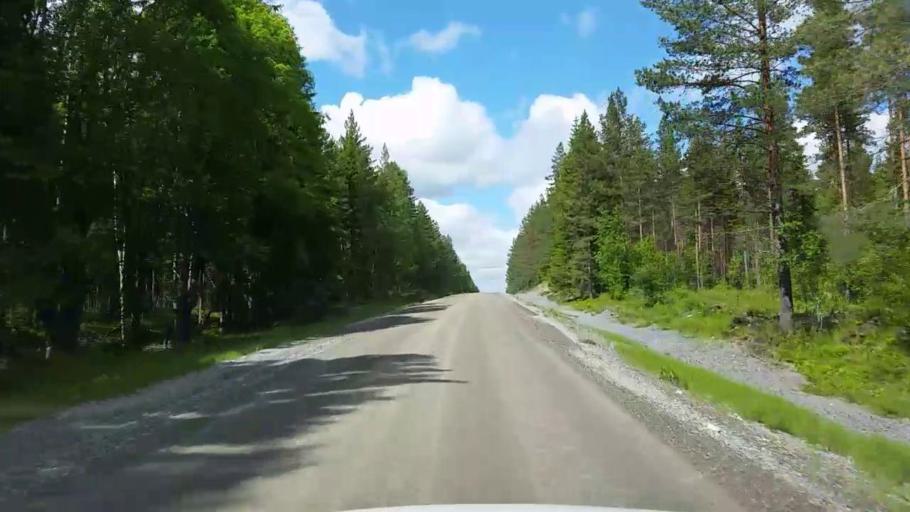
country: SE
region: Gaevleborg
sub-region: Bollnas Kommun
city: Vittsjo
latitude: 61.0475
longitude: 16.3344
